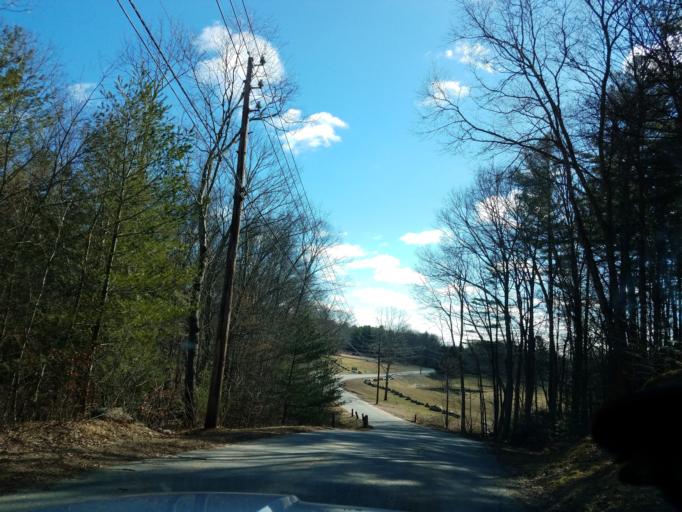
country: US
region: Connecticut
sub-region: Windham County
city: Putnam
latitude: 41.8931
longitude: -71.9089
